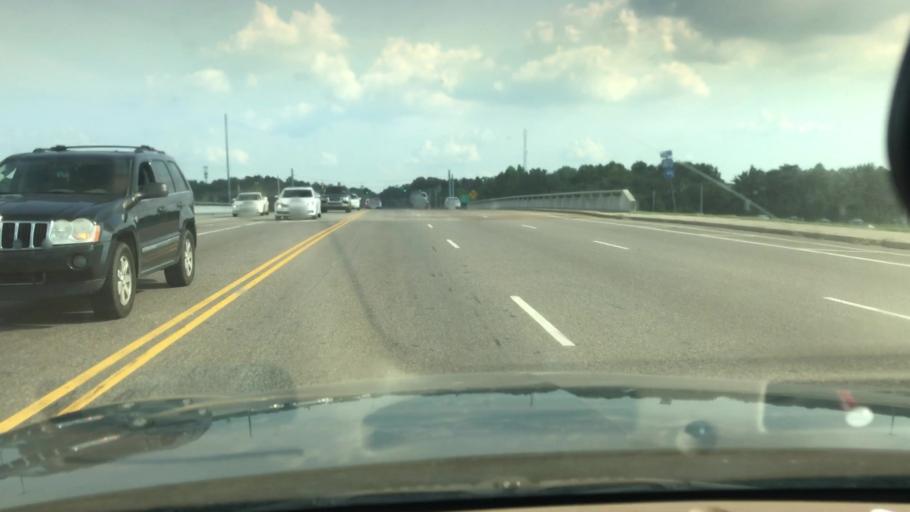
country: US
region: Tennessee
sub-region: Shelby County
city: Bartlett
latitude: 35.1760
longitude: -89.8364
